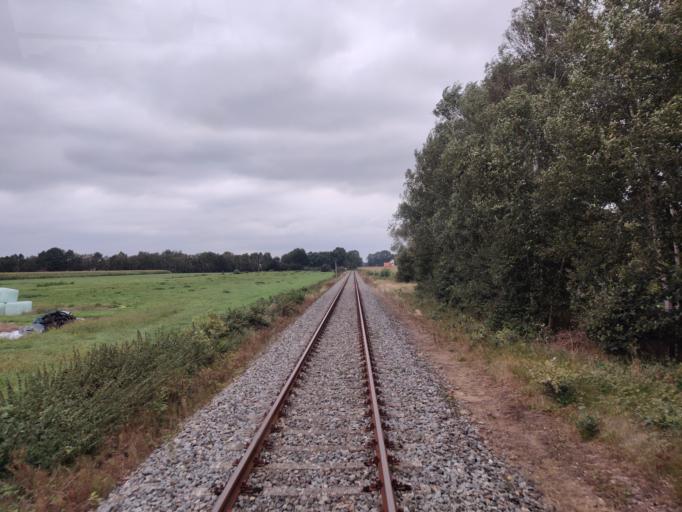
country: DE
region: Lower Saxony
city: Vollersode
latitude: 53.3159
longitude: 8.9759
